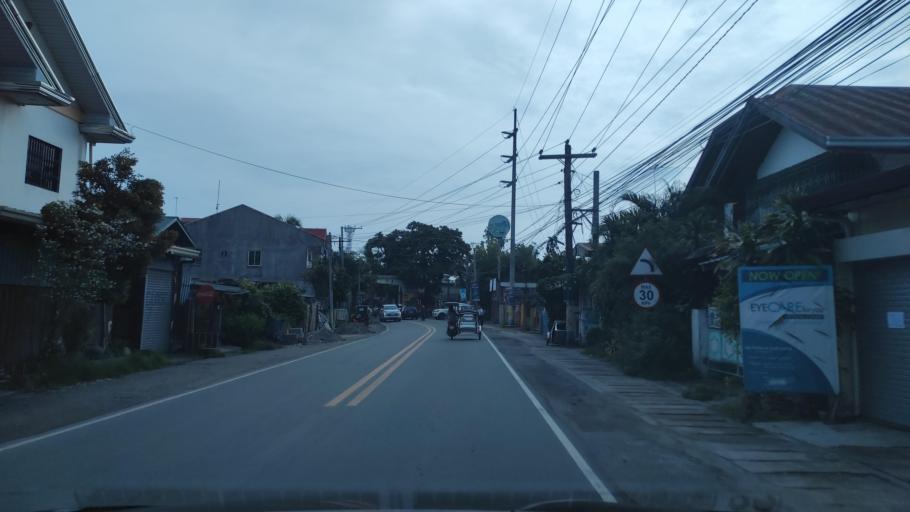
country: PH
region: Central Luzon
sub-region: Province of Pampanga
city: Santa Ana
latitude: 15.1177
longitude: 120.7753
